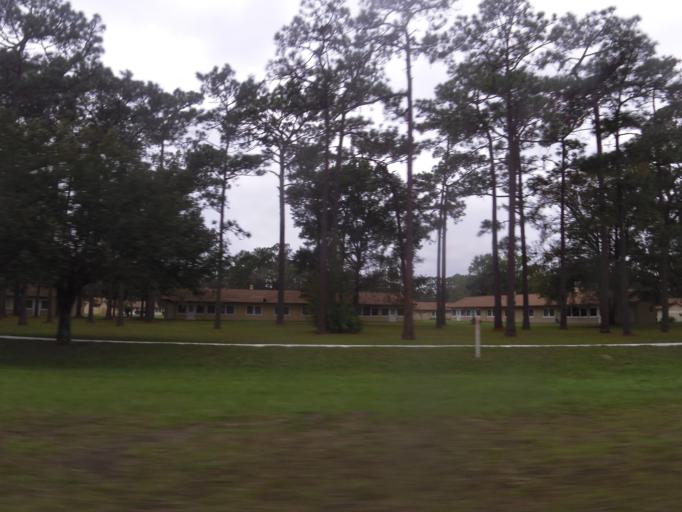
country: US
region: Florida
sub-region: Duval County
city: Baldwin
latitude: 30.2345
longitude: -81.8897
